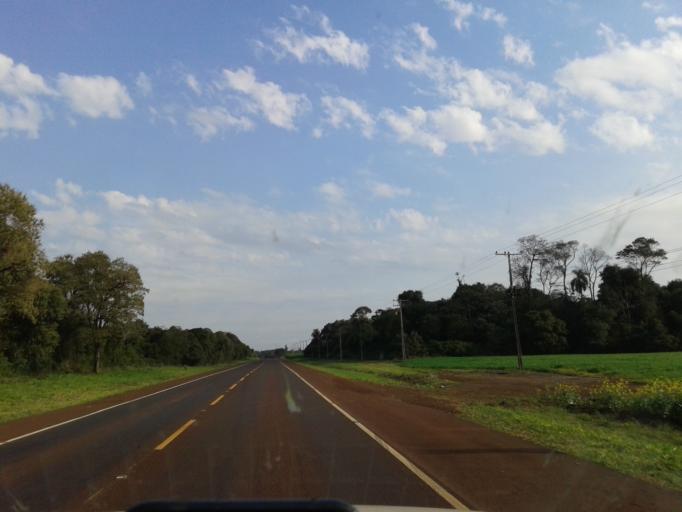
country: PY
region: Itapua
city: Edelira
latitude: -26.7798
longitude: -55.3948
